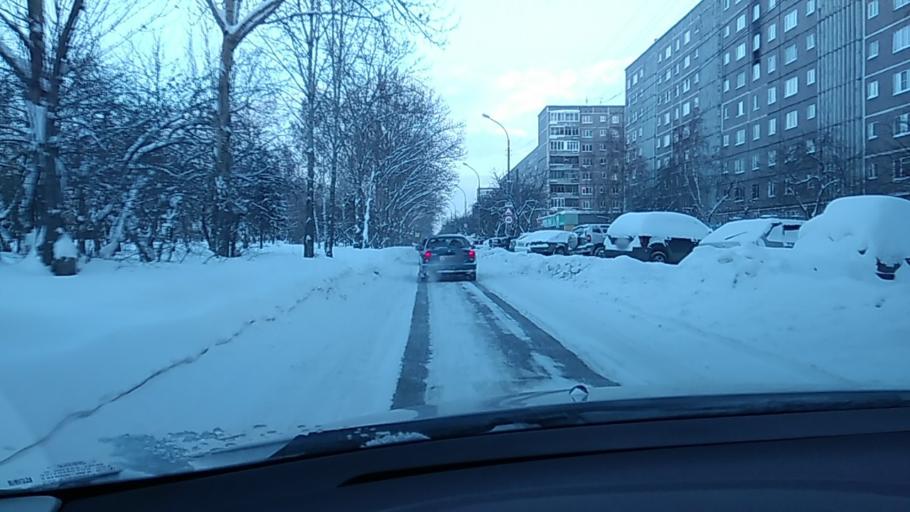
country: RU
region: Sverdlovsk
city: Sovkhoznyy
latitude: 56.8044
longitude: 60.5777
